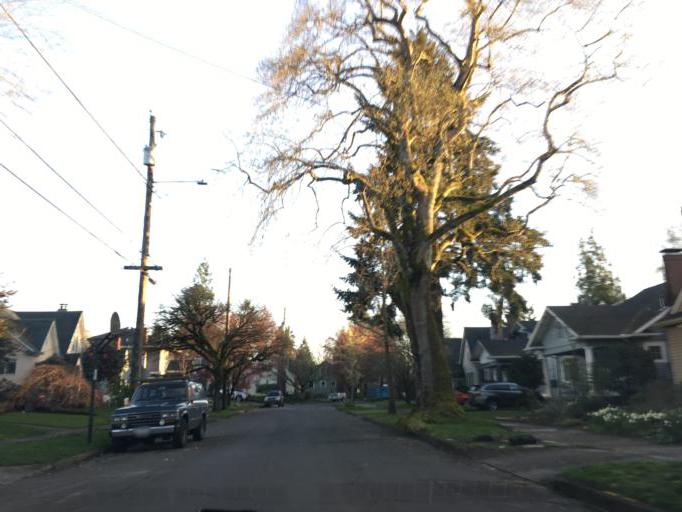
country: US
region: Oregon
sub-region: Multnomah County
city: Portland
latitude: 45.5416
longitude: -122.6340
